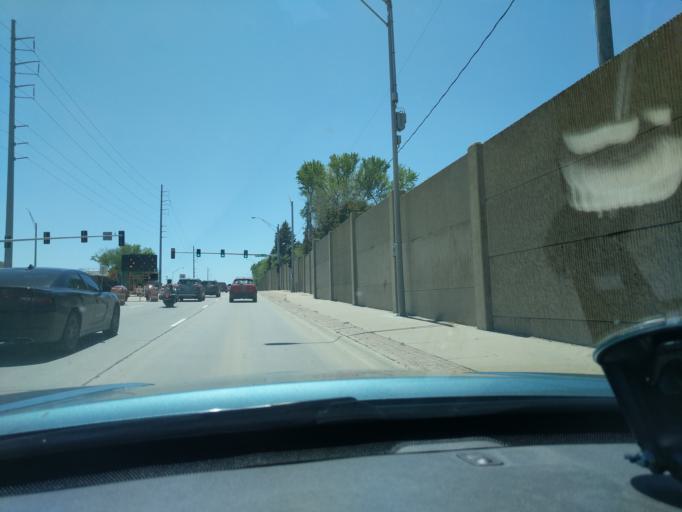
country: US
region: Nebraska
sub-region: Douglas County
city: Ralston
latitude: 41.2324
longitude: -96.0241
